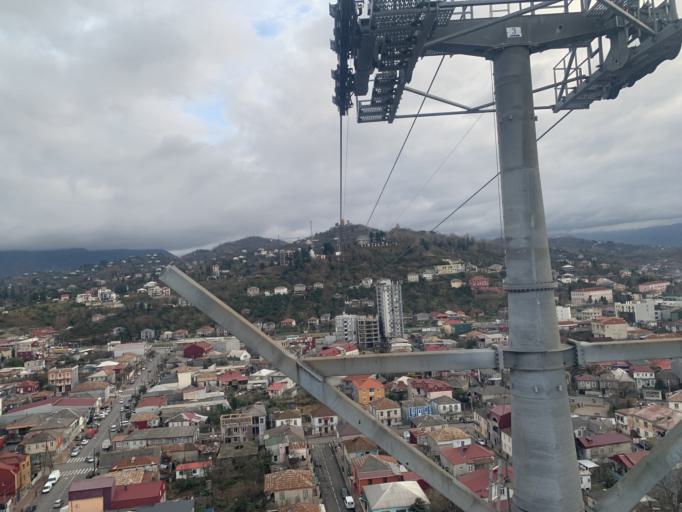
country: GE
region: Ajaria
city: Batumi
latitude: 41.6430
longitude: 41.6479
